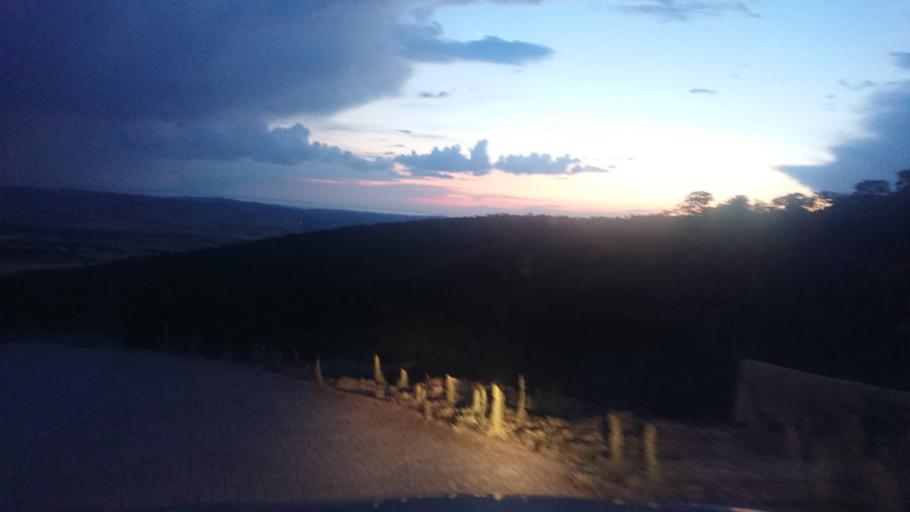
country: TR
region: Aksaray
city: Ortakoy
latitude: 38.6439
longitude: 34.0234
